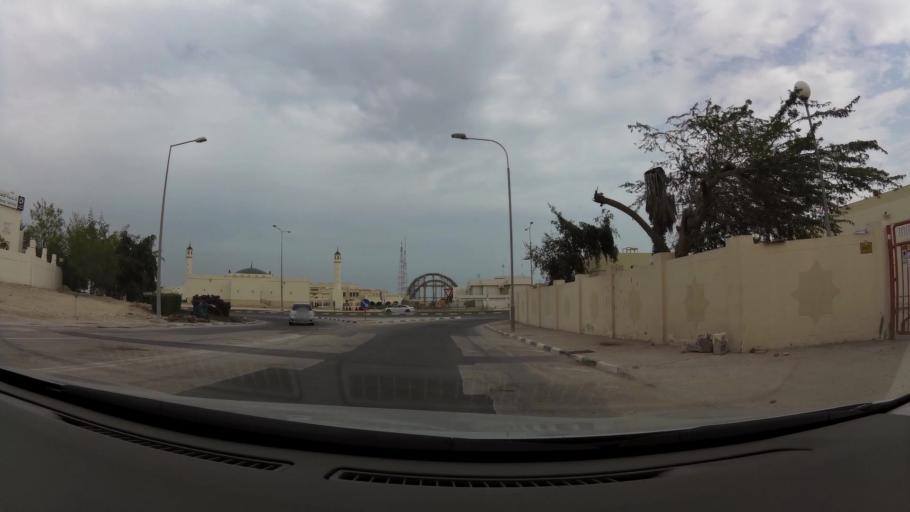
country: QA
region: Baladiyat ad Dawhah
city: Doha
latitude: 25.3352
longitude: 51.5051
